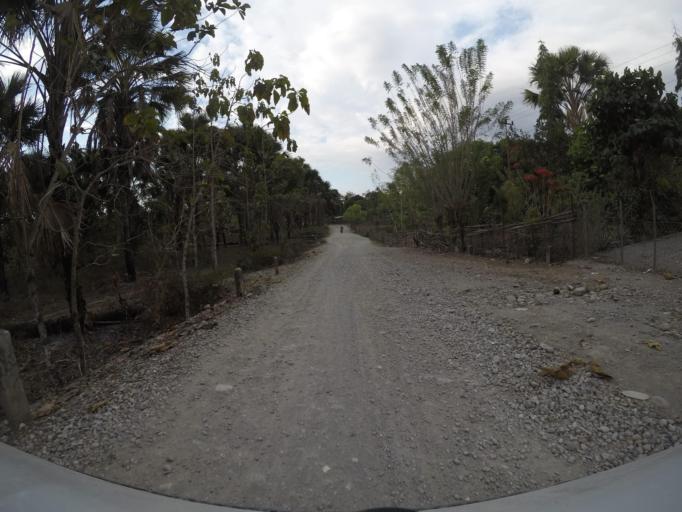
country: TL
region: Bobonaro
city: Maliana
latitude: -8.8756
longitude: 125.2120
